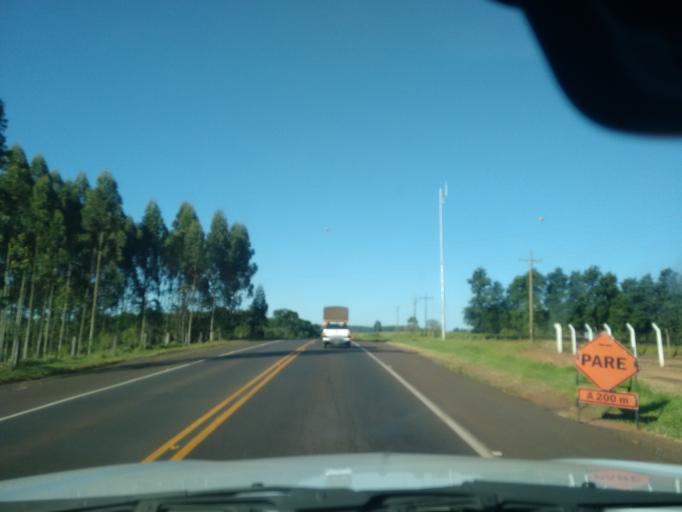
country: PY
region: Canindeyu
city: Salto del Guaira
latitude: -23.9617
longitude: -54.3214
